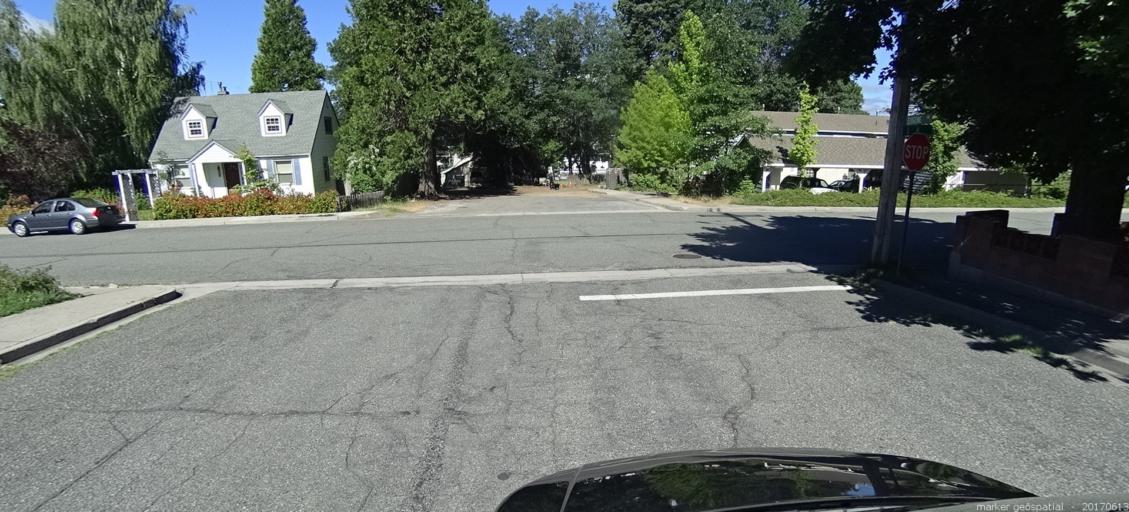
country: US
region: California
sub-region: Siskiyou County
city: Mount Shasta
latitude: 41.3086
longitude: -122.3094
